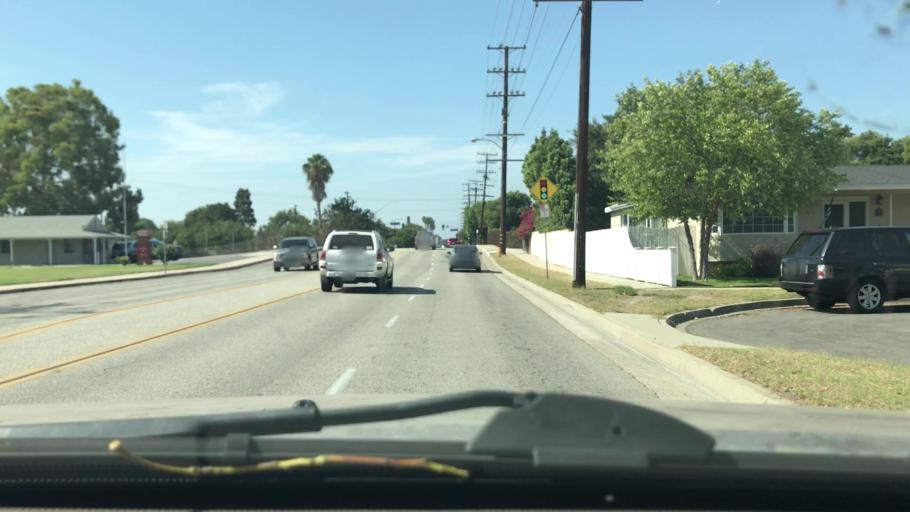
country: US
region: California
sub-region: Orange County
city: Rossmoor
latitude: 33.8016
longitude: -118.1079
